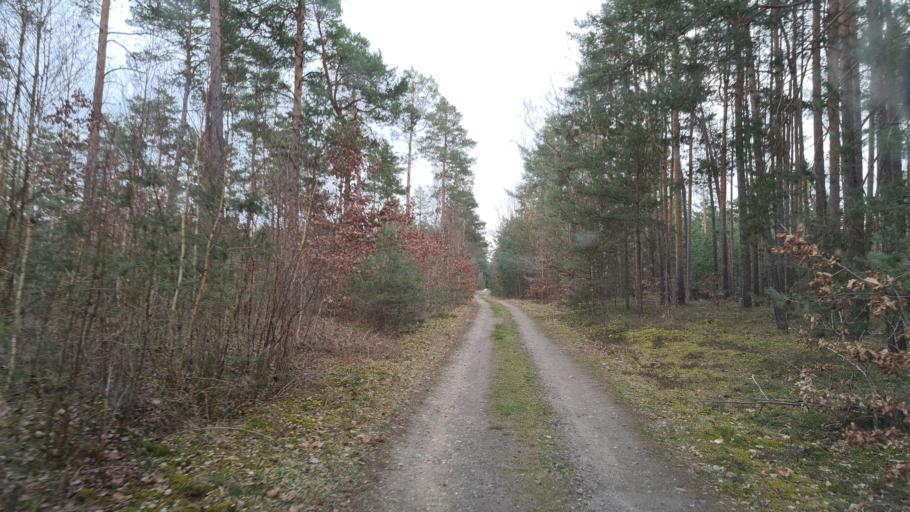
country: DE
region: Brandenburg
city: Schonborn
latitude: 51.5514
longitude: 13.4948
